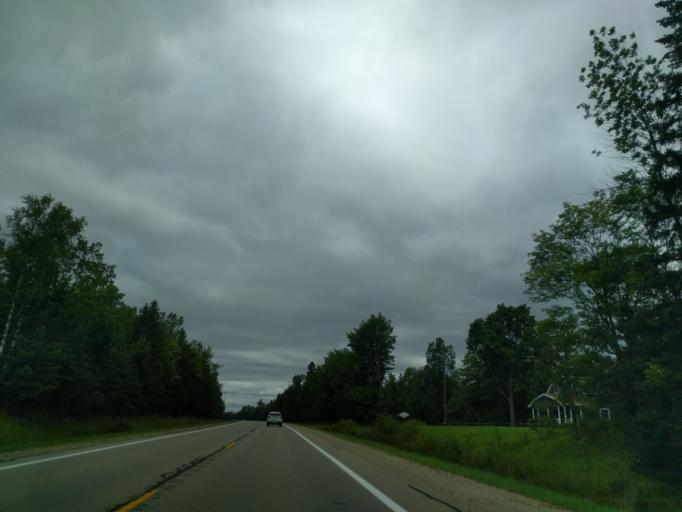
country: US
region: Michigan
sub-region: Delta County
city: Escanaba
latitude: 45.4587
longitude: -87.3305
